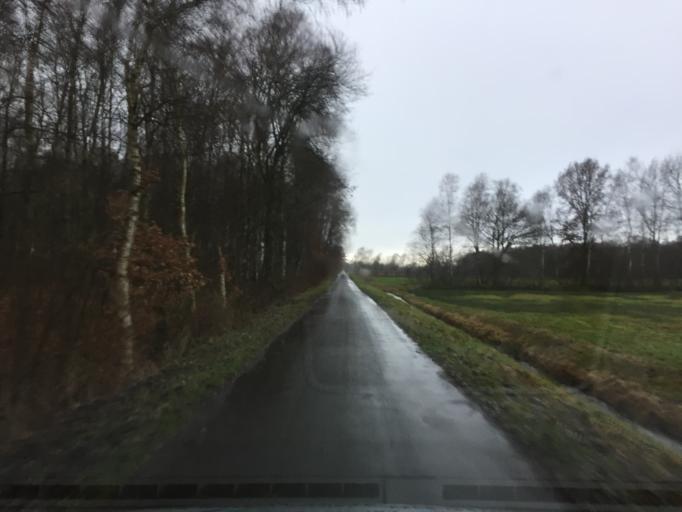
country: DE
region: Lower Saxony
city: Hassel
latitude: 52.6556
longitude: 8.8524
